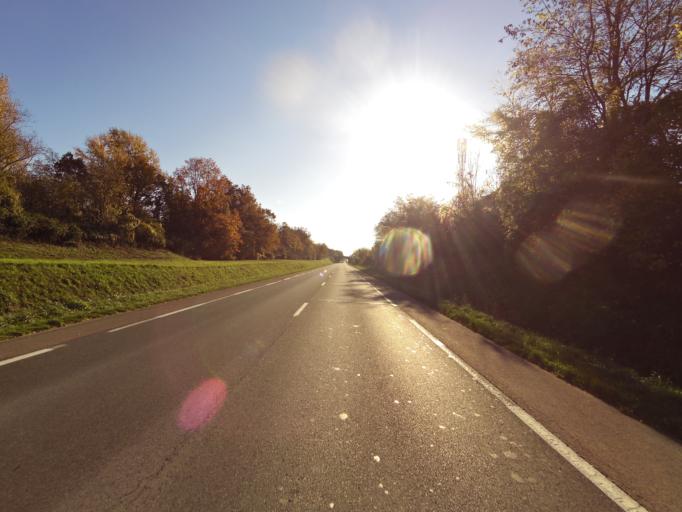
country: FR
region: Champagne-Ardenne
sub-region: Departement de l'Aube
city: Breviandes
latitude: 48.2557
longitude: 4.1031
